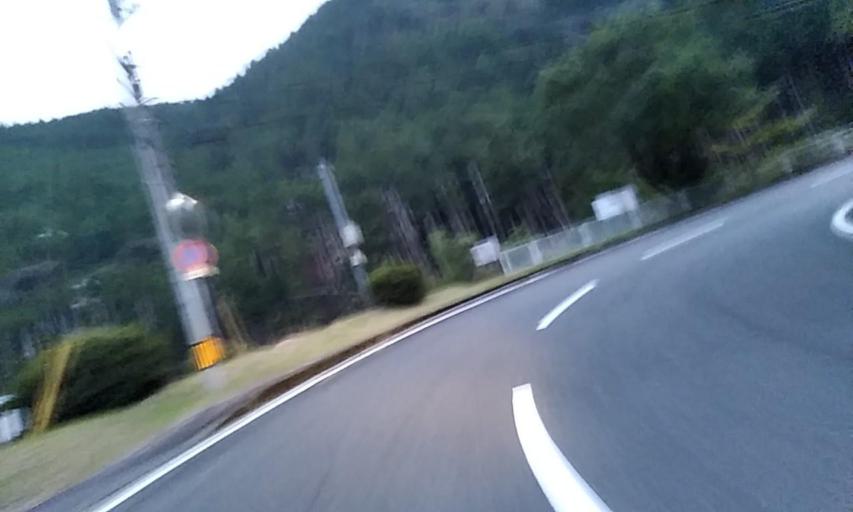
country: JP
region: Wakayama
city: Shingu
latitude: 33.7375
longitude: 135.9350
